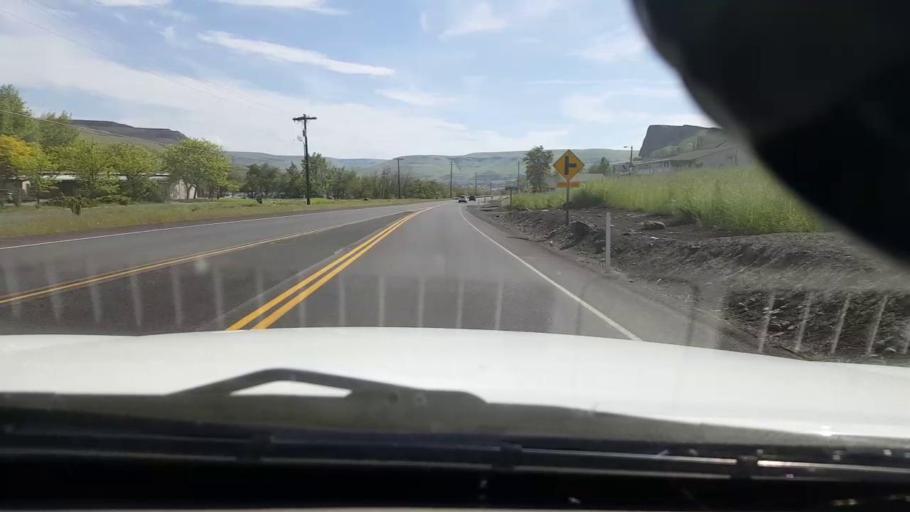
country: US
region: Washington
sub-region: Asotin County
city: West Clarkston-Highland
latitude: 46.3815
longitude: -117.0508
